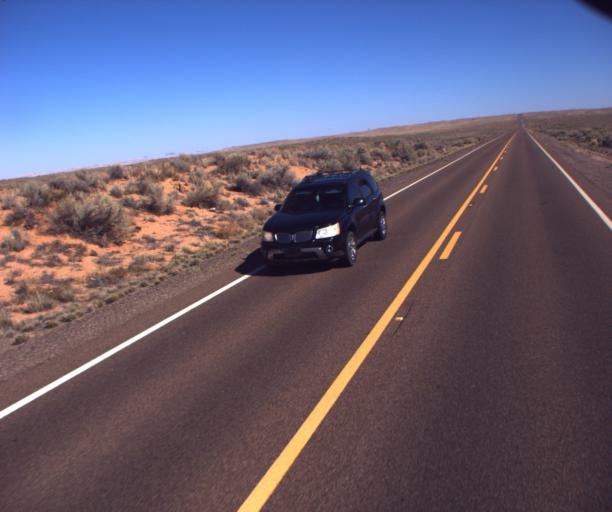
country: US
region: Arizona
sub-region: Navajo County
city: Winslow
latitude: 35.0384
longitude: -110.6124
